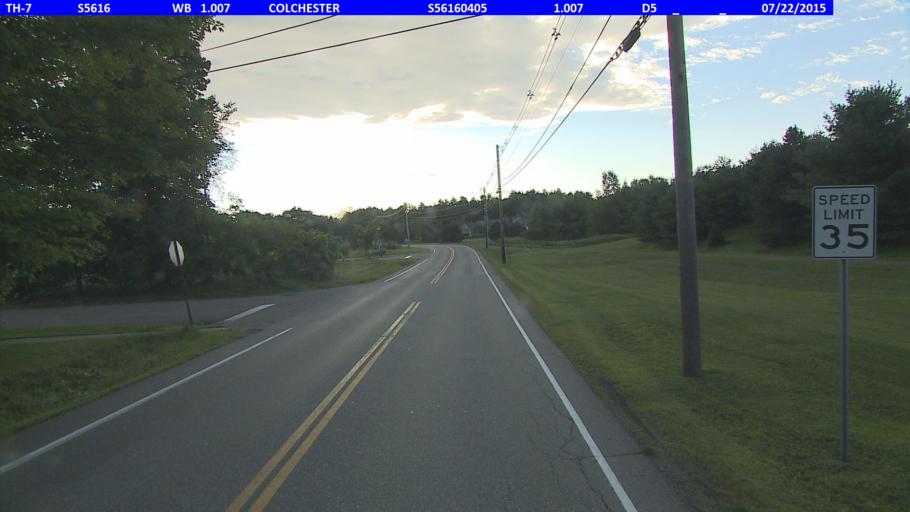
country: US
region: Vermont
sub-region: Chittenden County
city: Colchester
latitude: 44.5235
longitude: -73.1539
